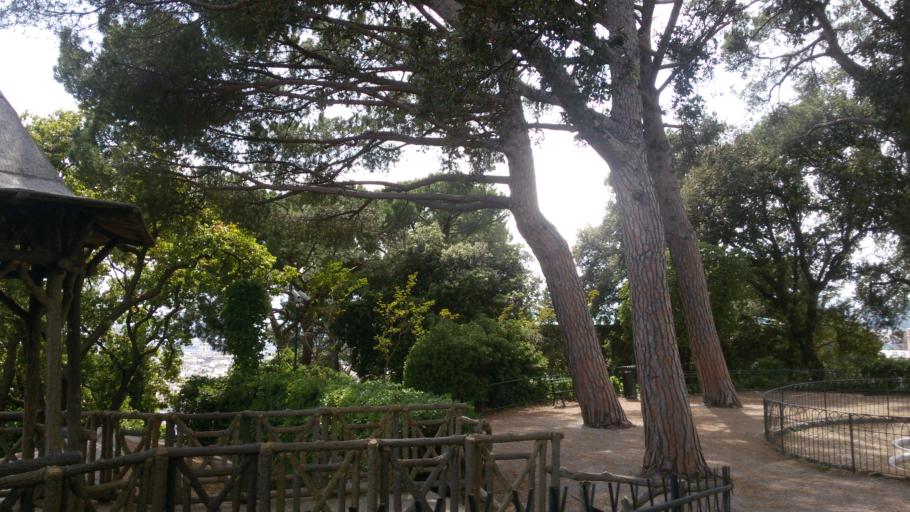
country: IT
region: Liguria
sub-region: Provincia di Genova
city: Genoa
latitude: 44.4114
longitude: 8.9369
